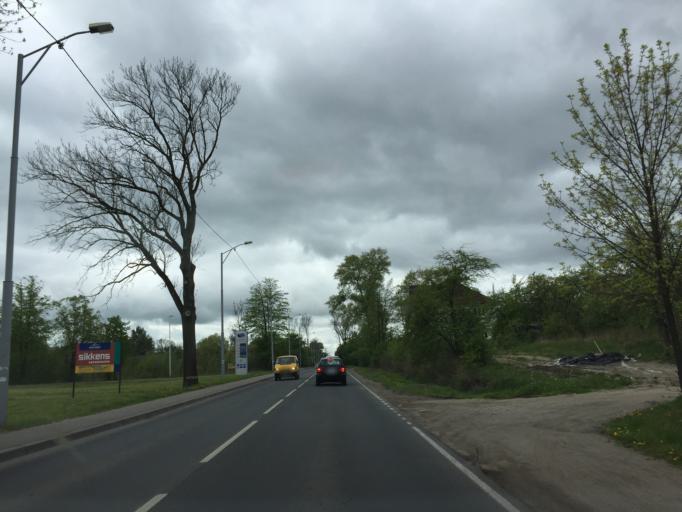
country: RU
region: Kaliningrad
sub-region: Gorod Kaliningrad
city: Kaliningrad
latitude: 54.6746
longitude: 20.4392
